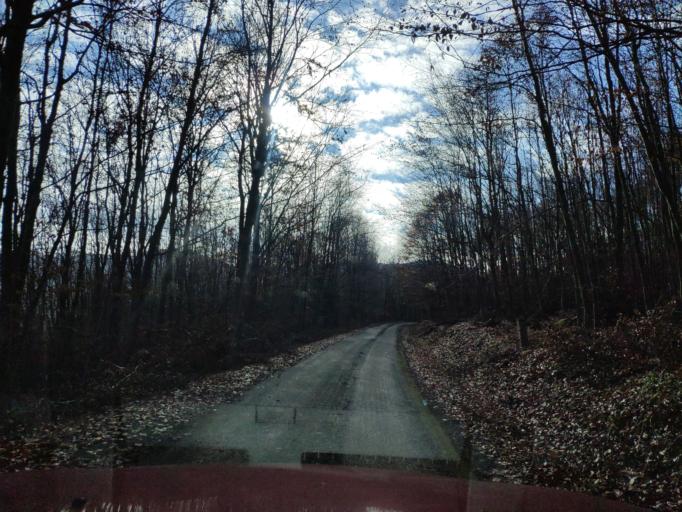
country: HU
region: Borsod-Abauj-Zemplen
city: Gonc
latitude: 48.6066
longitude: 21.4574
